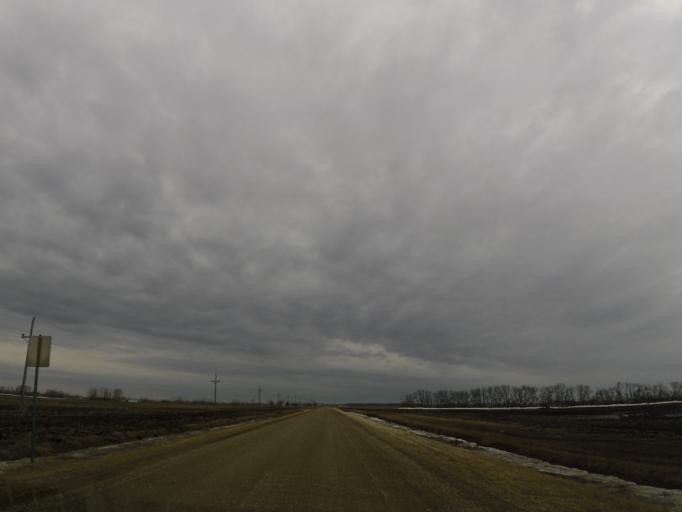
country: US
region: North Dakota
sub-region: Walsh County
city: Grafton
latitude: 48.4198
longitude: -97.4372
